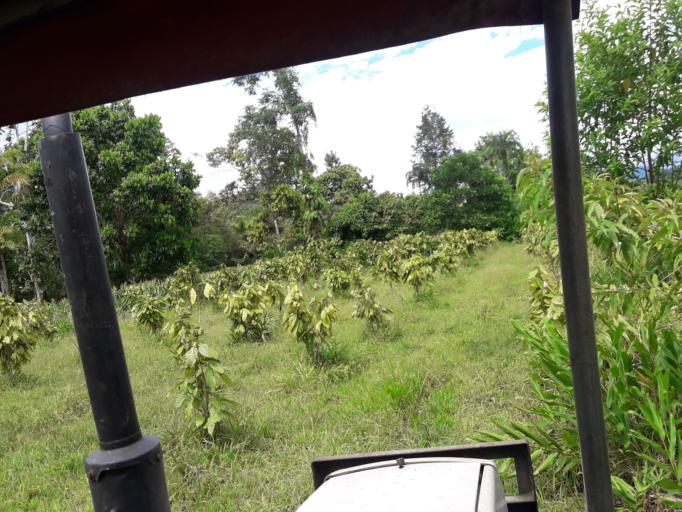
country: EC
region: Napo
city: Tena
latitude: -1.0696
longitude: -77.7958
